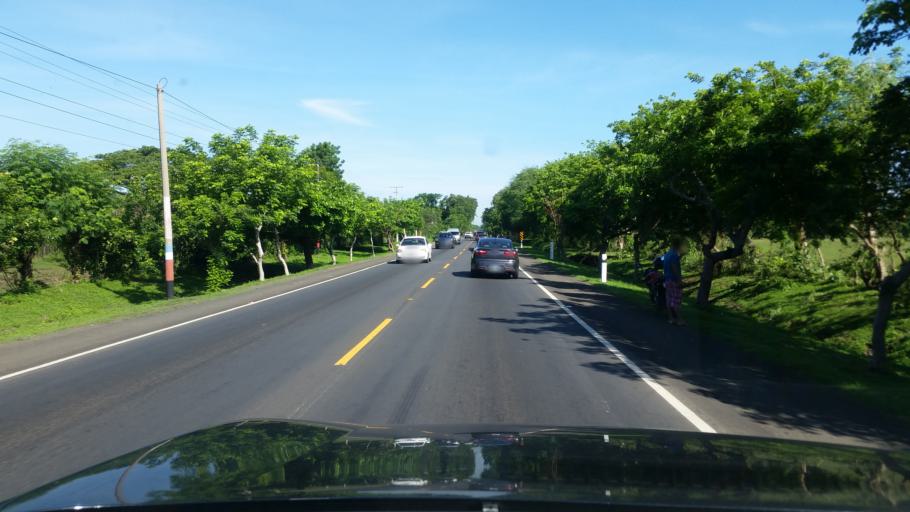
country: NI
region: Chinandega
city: Chichigalpa
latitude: 12.5935
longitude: -87.0280
